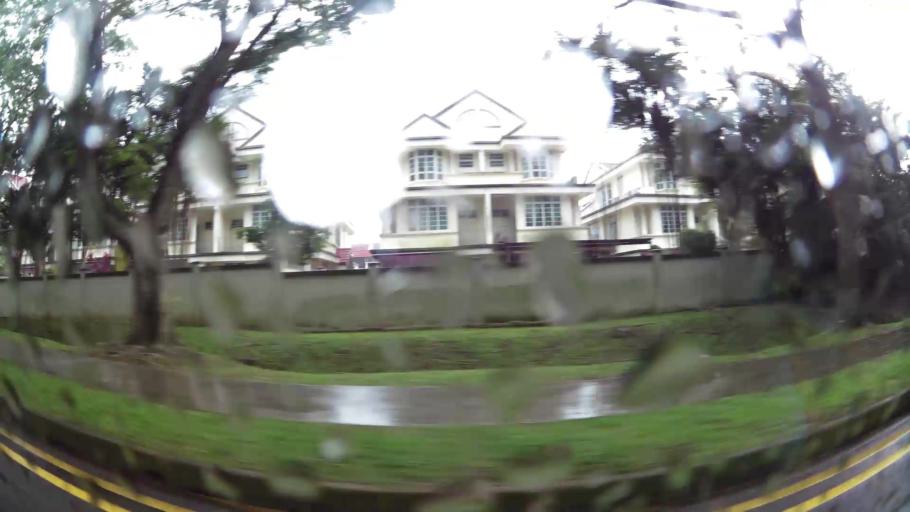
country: MY
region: Johor
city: Kampung Pasir Gudang Baru
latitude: 1.3922
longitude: 103.8524
